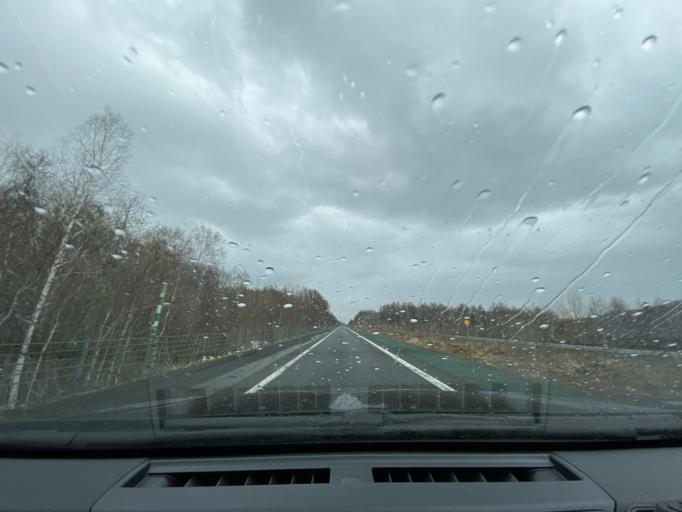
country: JP
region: Hokkaido
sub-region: Asahikawa-shi
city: Asahikawa
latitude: 43.9851
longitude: 142.4570
